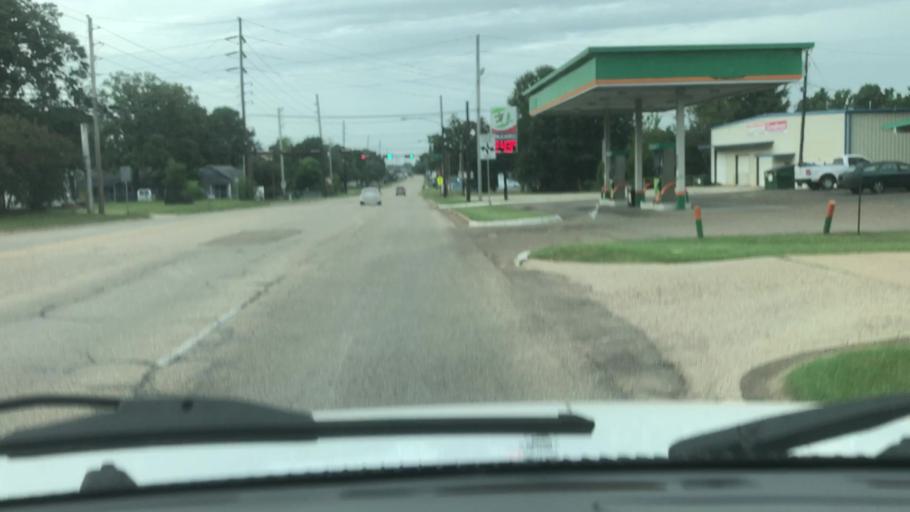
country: US
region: Texas
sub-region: Bowie County
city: Wake Village
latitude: 33.4319
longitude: -94.0805
